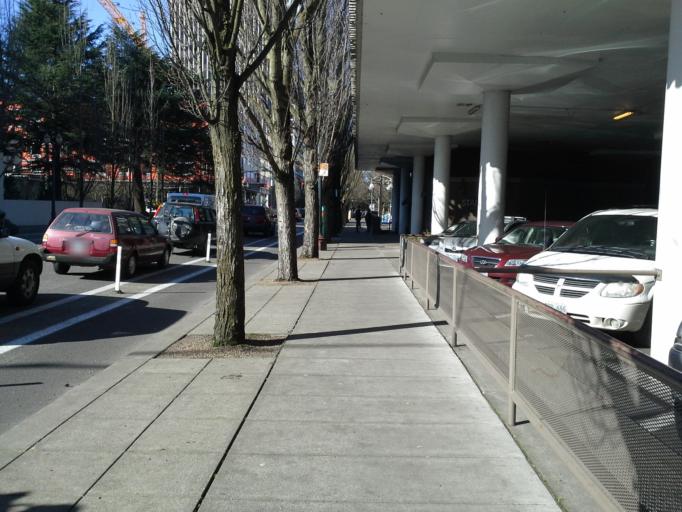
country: US
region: Oregon
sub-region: Multnomah County
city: Portland
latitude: 45.5317
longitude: -122.6552
